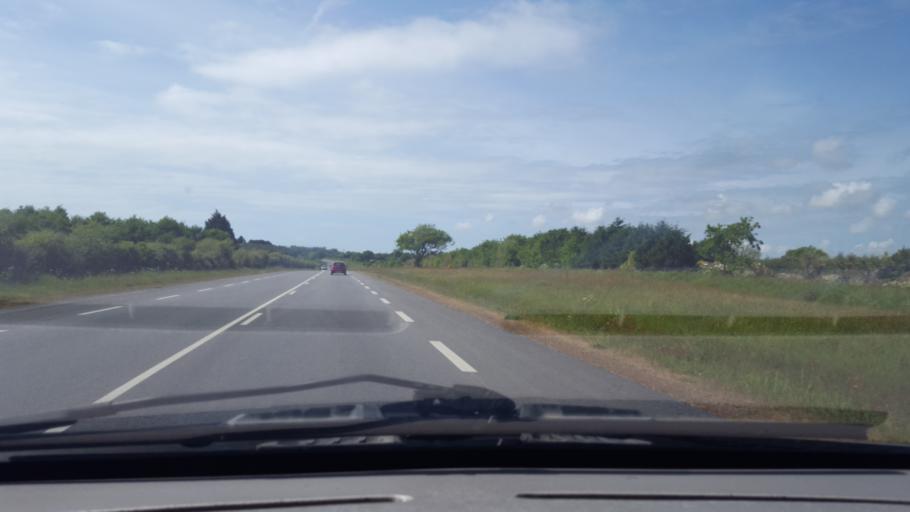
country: FR
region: Pays de la Loire
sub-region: Departement de la Loire-Atlantique
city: Les Moutiers-en-Retz
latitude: 47.0721
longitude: -1.9945
